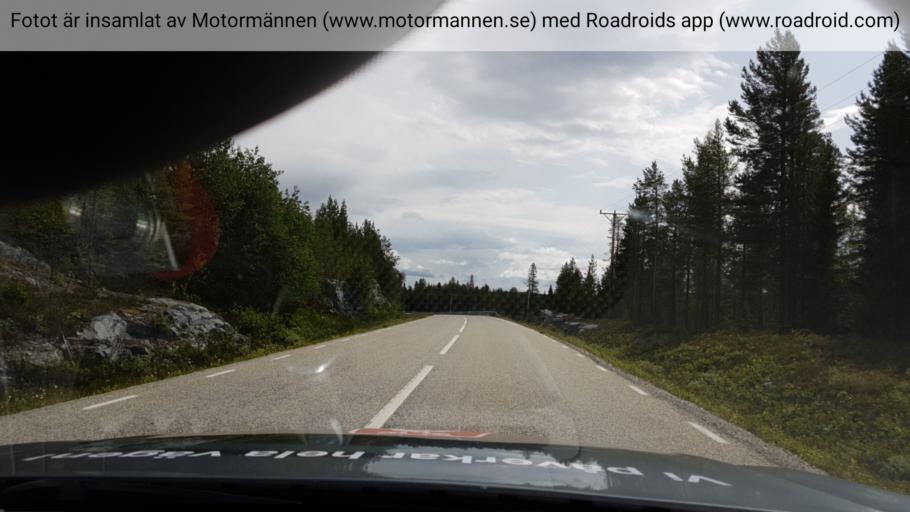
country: SE
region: Jaemtland
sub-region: Are Kommun
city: Jarpen
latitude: 62.7783
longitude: 13.7007
